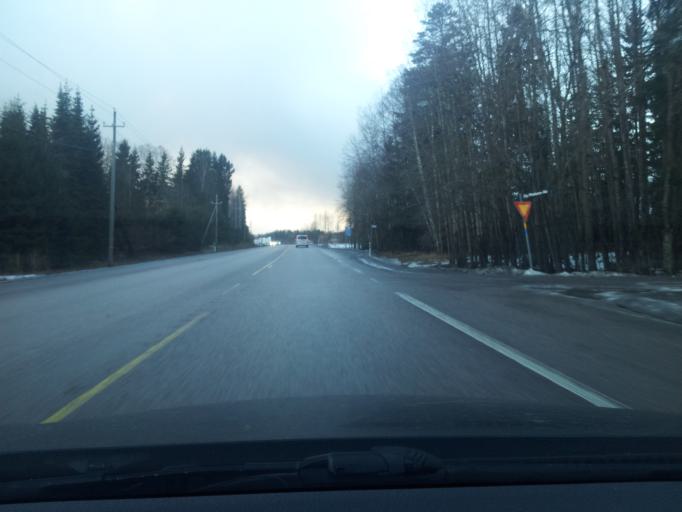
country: FI
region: Uusimaa
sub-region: Helsinki
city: Espoo
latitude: 60.1714
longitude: 24.5536
